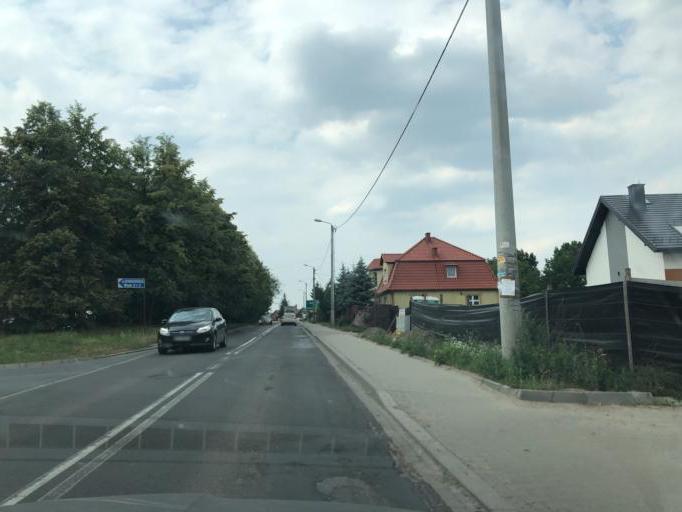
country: PL
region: Lesser Poland Voivodeship
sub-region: Powiat wielicki
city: Wieliczka
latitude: 49.9876
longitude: 20.0439
